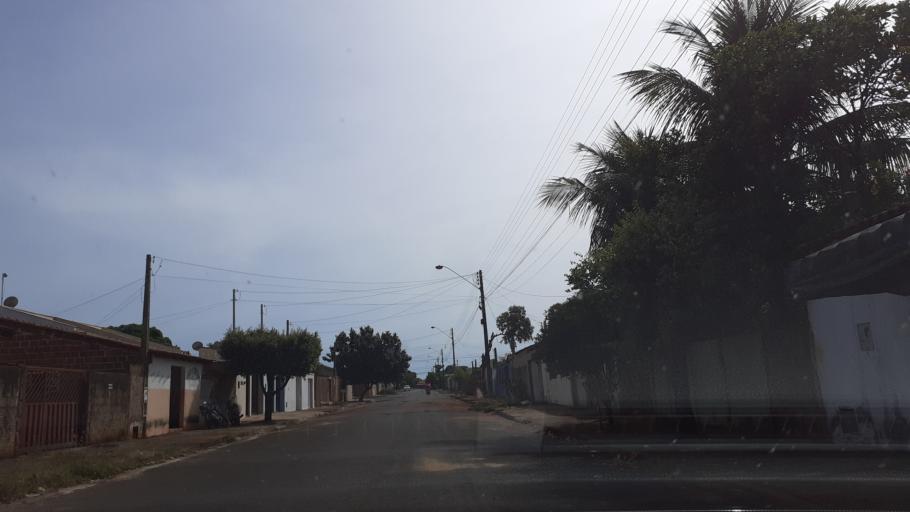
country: BR
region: Goias
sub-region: Itumbiara
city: Itumbiara
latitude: -18.4226
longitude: -49.2448
